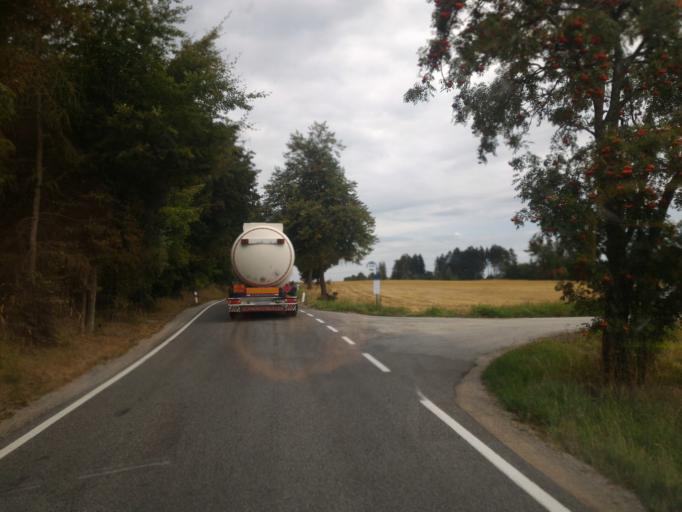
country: CZ
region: Vysocina
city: Zeletava
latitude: 49.1947
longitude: 15.6047
